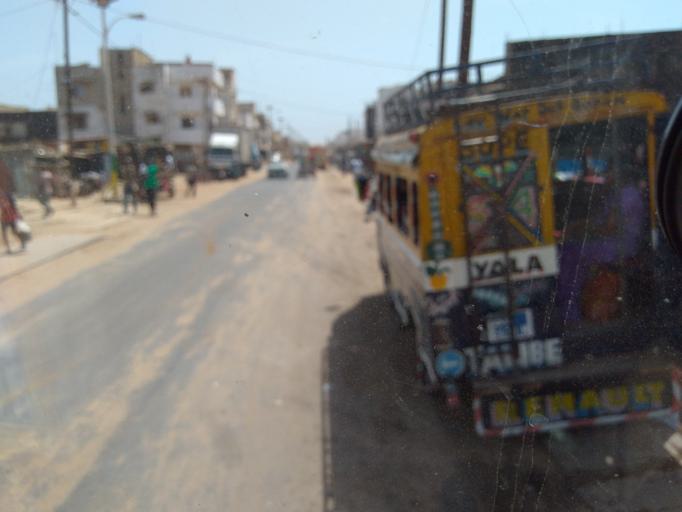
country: SN
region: Dakar
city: Pikine
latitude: 14.7868
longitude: -17.3472
